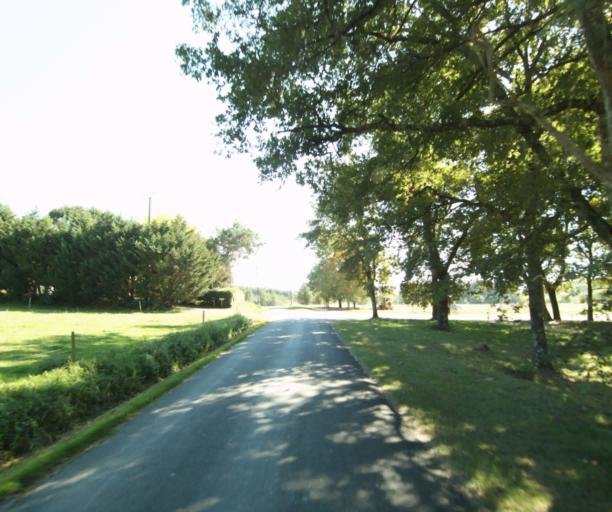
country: FR
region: Midi-Pyrenees
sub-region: Departement du Gers
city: Cazaubon
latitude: 43.9362
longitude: -0.0332
